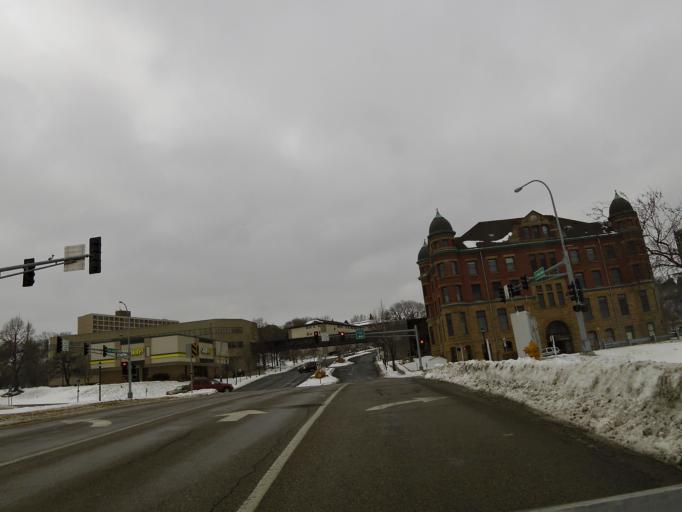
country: US
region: Minnesota
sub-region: Dakota County
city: South Saint Paul
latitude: 44.8934
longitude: -93.0338
